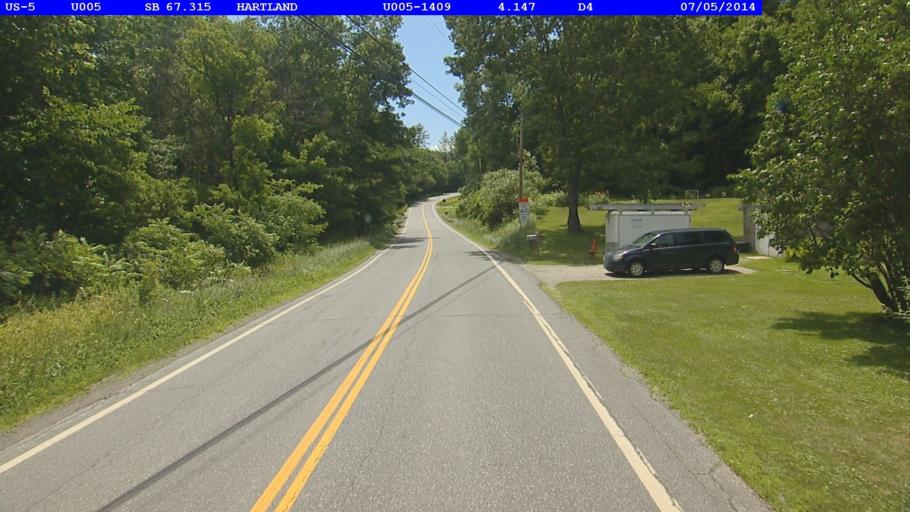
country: US
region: Vermont
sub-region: Windsor County
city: Windsor
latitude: 43.5708
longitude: -72.3831
